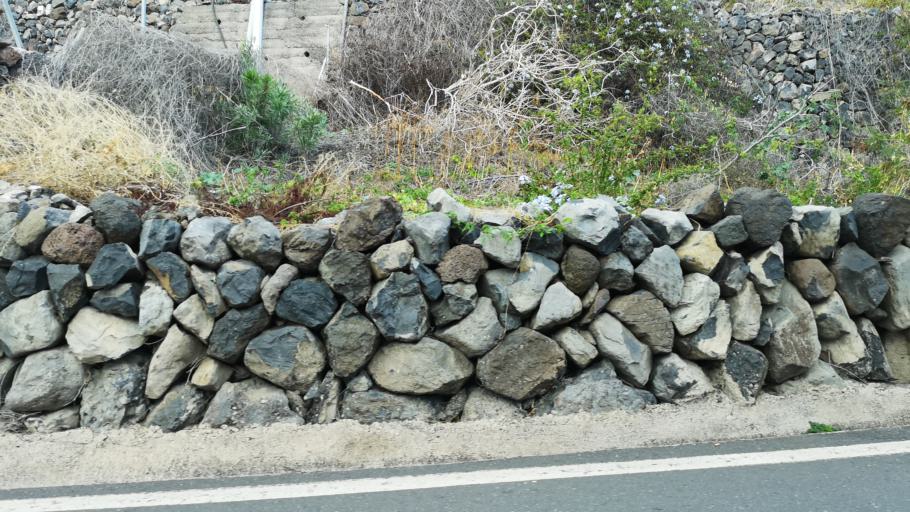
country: ES
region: Canary Islands
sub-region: Provincia de Santa Cruz de Tenerife
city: Hermigua
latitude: 28.1754
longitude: -17.1865
